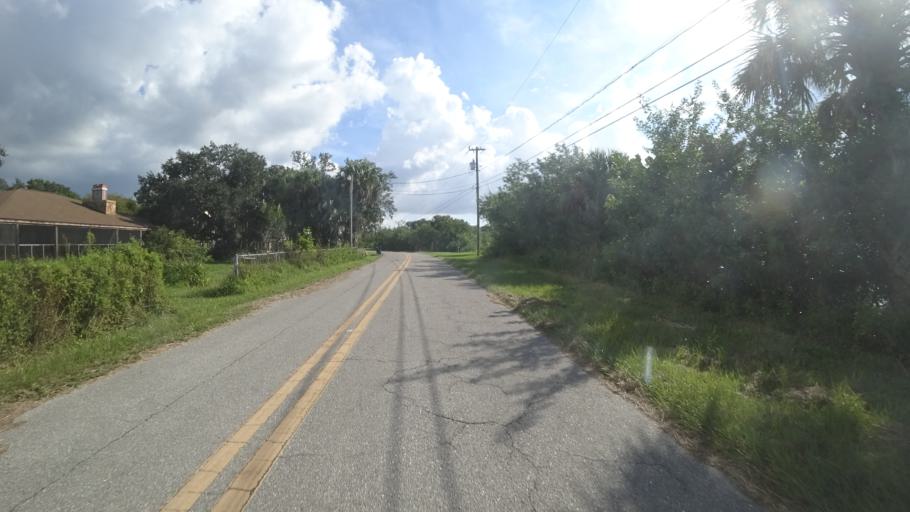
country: US
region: Florida
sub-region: Manatee County
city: Memphis
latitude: 27.5731
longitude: -82.5852
